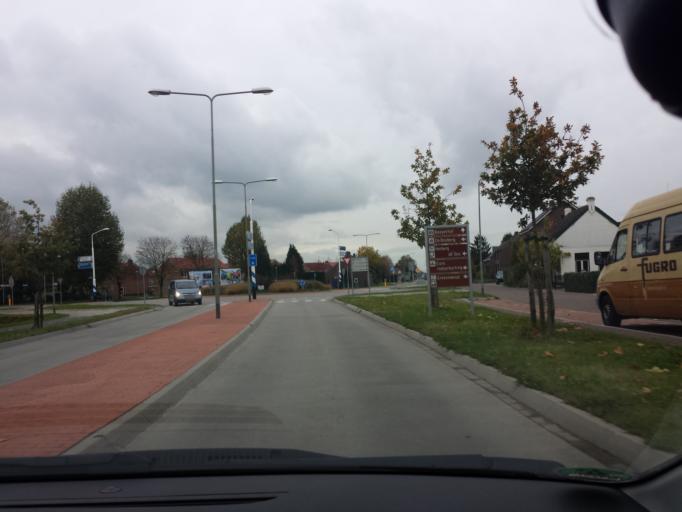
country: NL
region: Limburg
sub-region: Gemeente Beesel
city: Beesel
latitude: 51.2418
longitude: 6.0489
